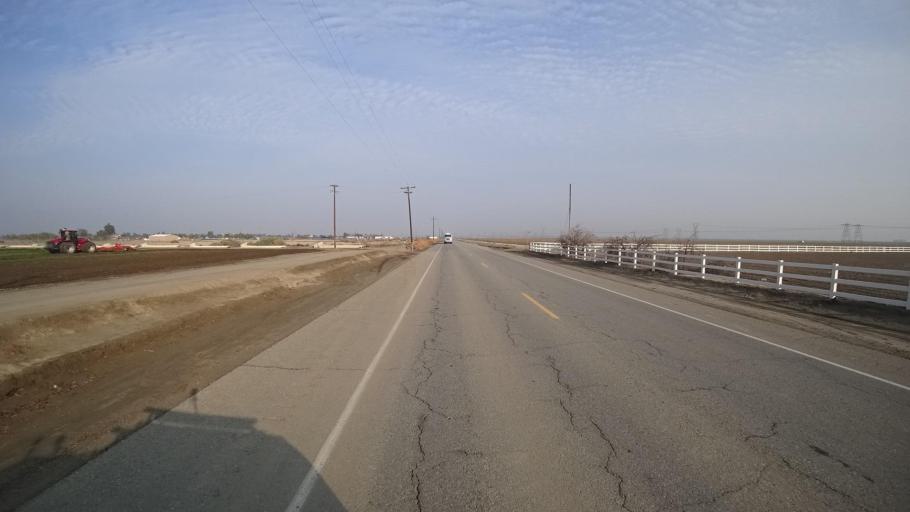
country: US
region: California
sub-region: Kern County
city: Weedpatch
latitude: 35.1651
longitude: -118.9147
